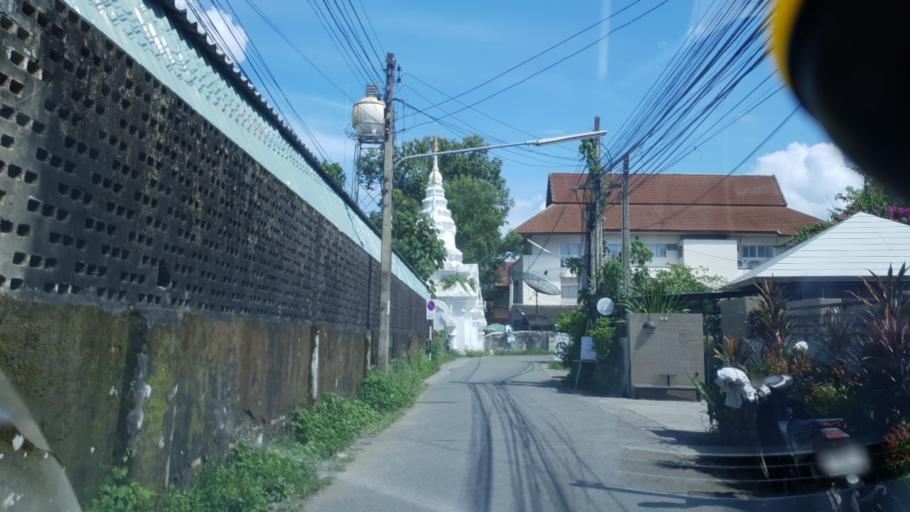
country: TH
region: Chiang Mai
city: Chiang Mai
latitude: 18.7875
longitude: 98.9669
